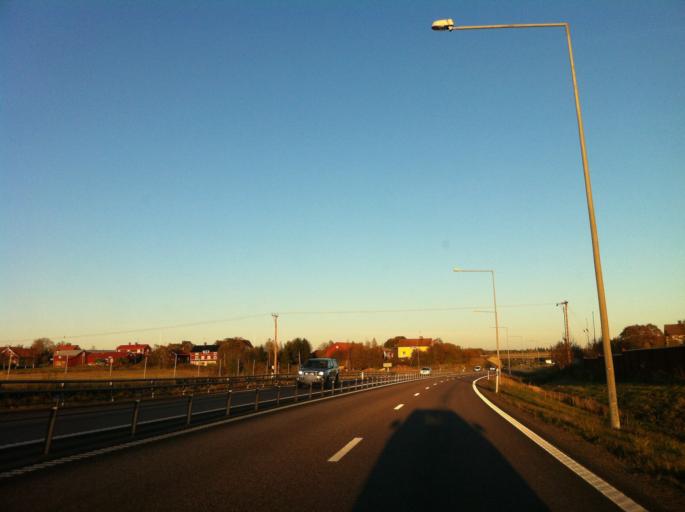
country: SE
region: Gaevleborg
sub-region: Sandvikens Kommun
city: Jarbo
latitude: 60.6077
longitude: 16.5973
